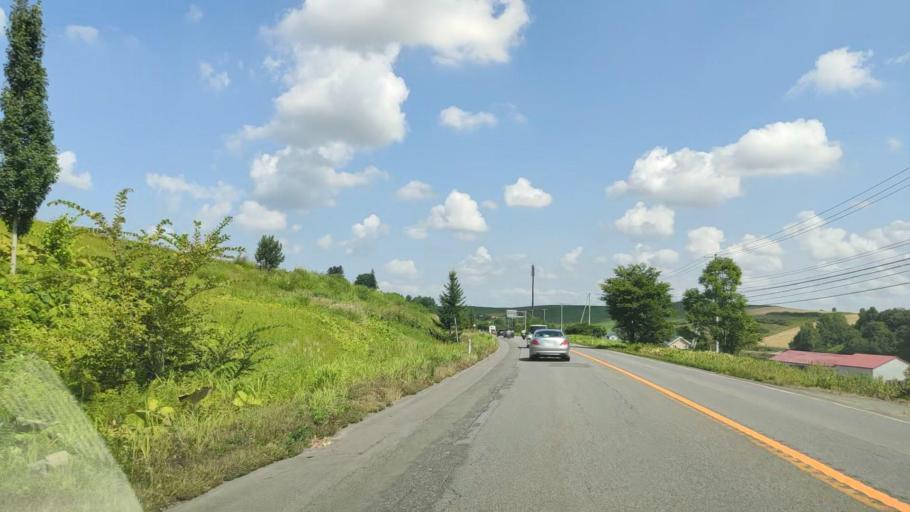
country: JP
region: Hokkaido
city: Shimo-furano
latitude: 43.5468
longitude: 142.4390
